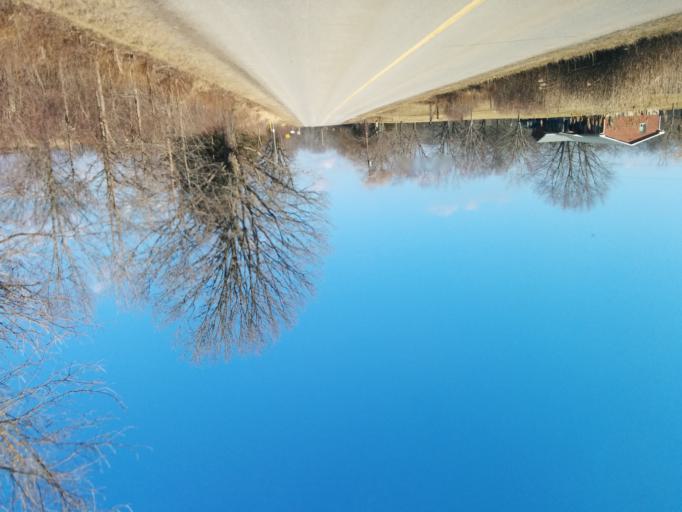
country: CA
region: Ontario
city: Brantford
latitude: 43.0080
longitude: -80.1208
